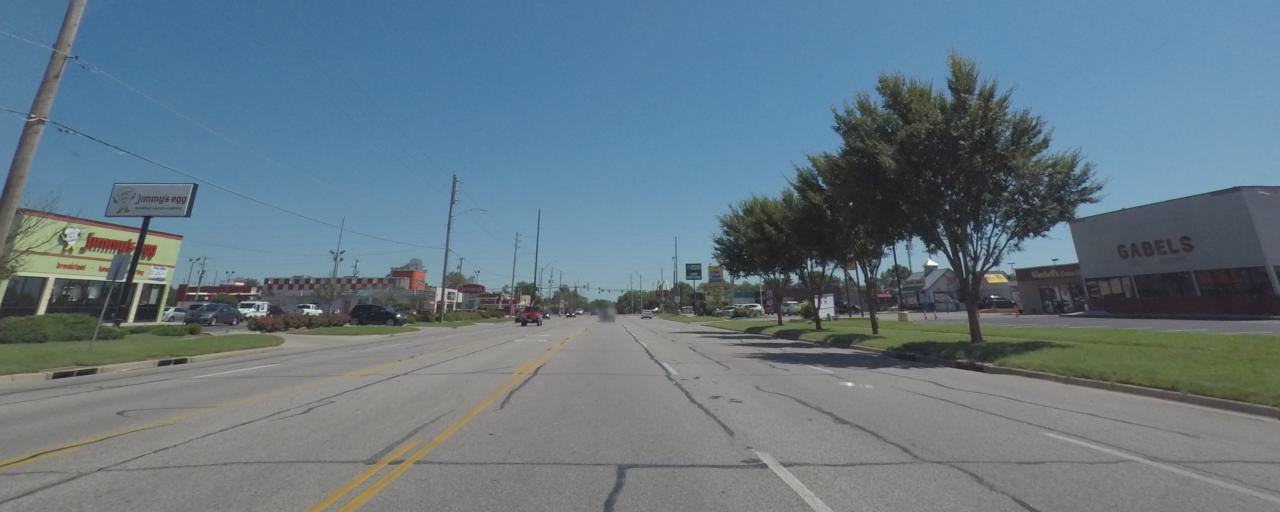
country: US
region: Kansas
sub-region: Sedgwick County
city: Wichita
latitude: 37.6515
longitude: -97.3547
